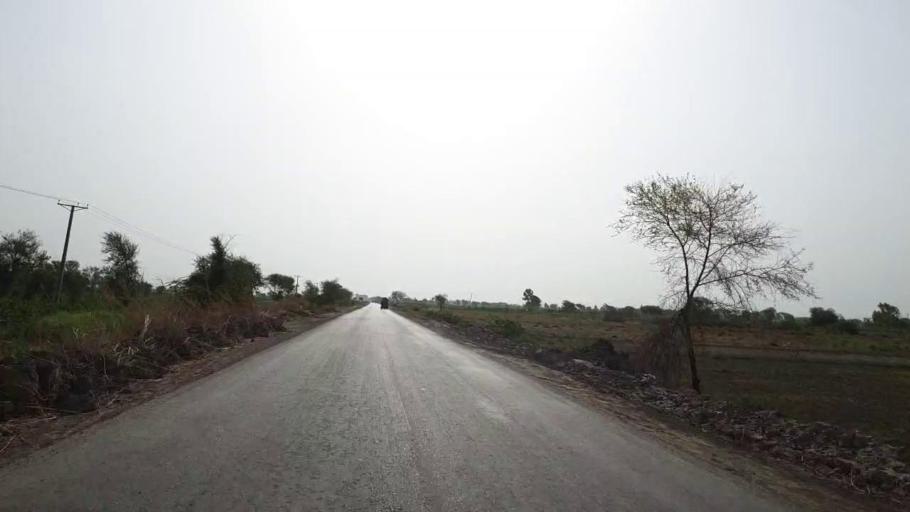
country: PK
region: Sindh
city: Jam Sahib
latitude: 26.2702
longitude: 68.5306
